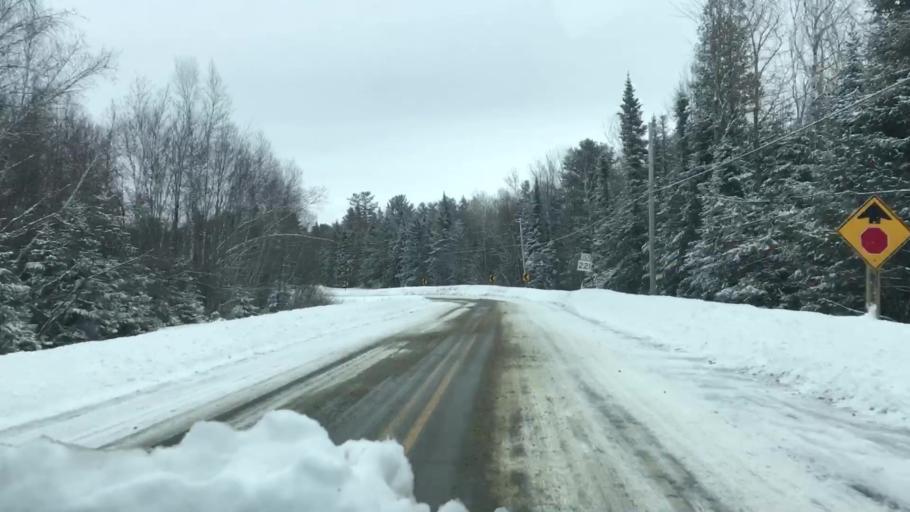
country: US
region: Maine
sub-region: Penobscot County
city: Hudson
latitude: 45.0218
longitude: -68.9160
